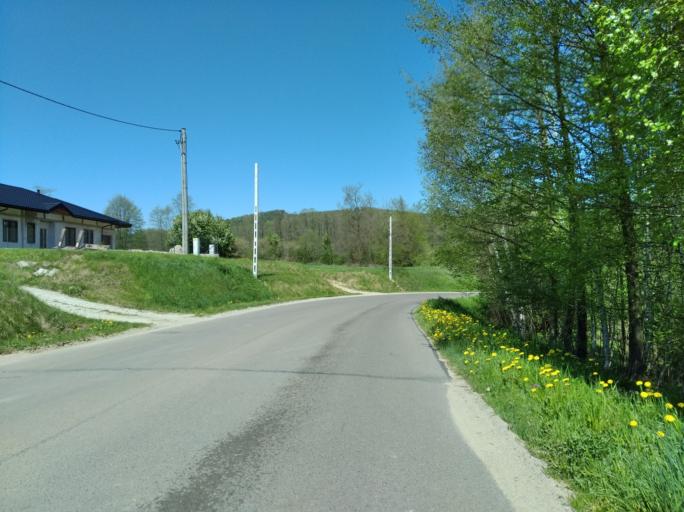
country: PL
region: Subcarpathian Voivodeship
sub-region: Powiat debicki
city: Brzostek
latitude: 49.9132
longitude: 21.3580
